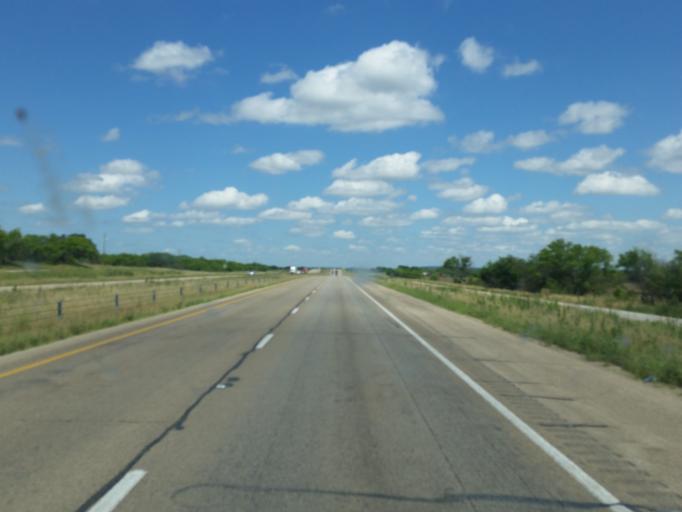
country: US
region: Texas
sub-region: Callahan County
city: Baird
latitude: 32.3871
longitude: -99.3091
